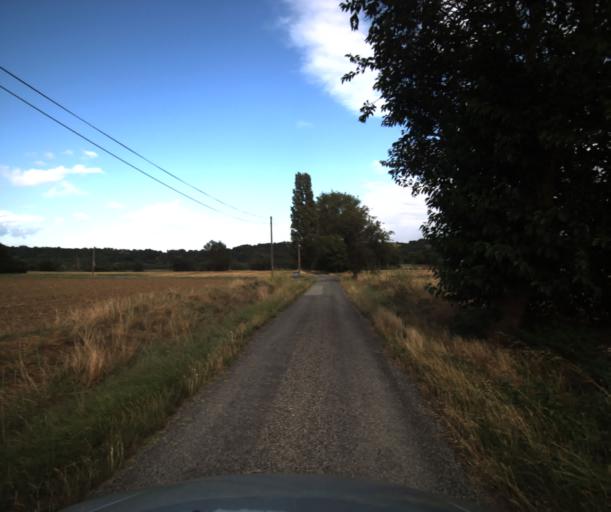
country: FR
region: Midi-Pyrenees
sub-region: Departement de la Haute-Garonne
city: Eaunes
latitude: 43.4372
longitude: 1.3152
